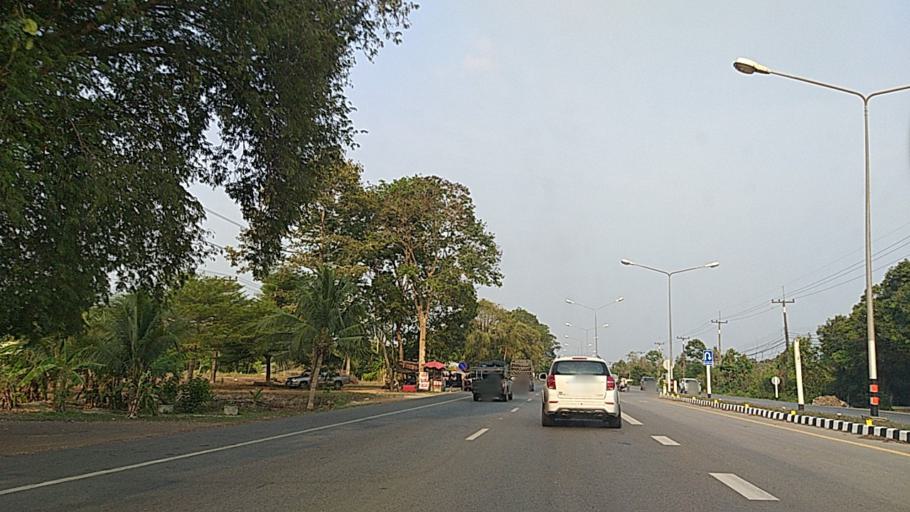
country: TH
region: Chanthaburi
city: Khlung
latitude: 12.4523
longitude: 102.2515
